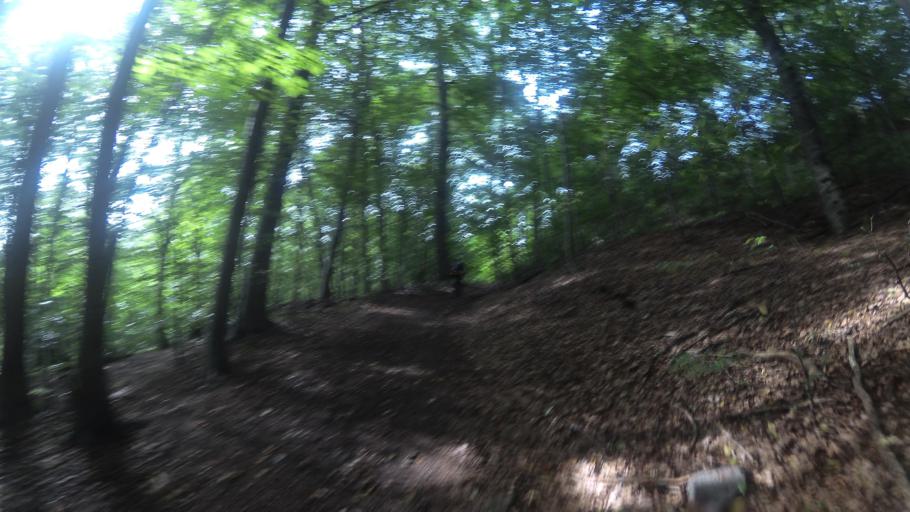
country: DE
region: Saarland
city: Sulzbach
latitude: 49.2879
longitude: 7.0835
